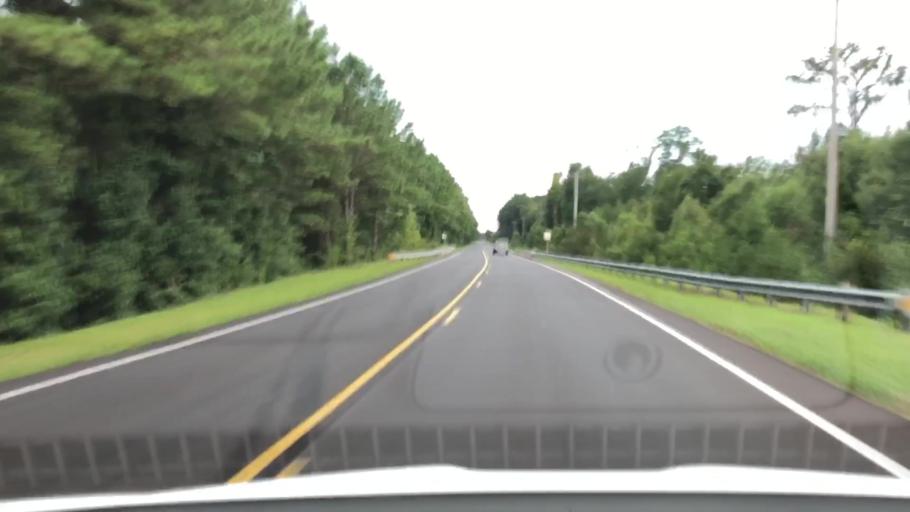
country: US
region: North Carolina
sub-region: Jones County
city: Maysville
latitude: 34.8710
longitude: -77.1957
